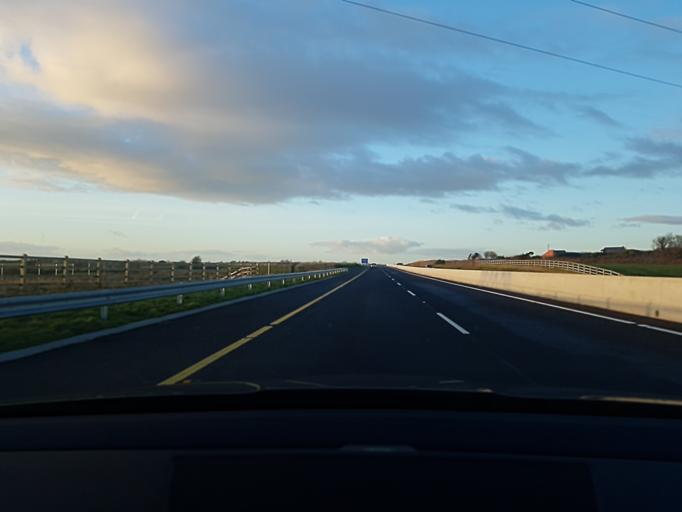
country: IE
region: Connaught
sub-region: County Galway
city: Athenry
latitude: 53.3803
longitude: -8.7977
